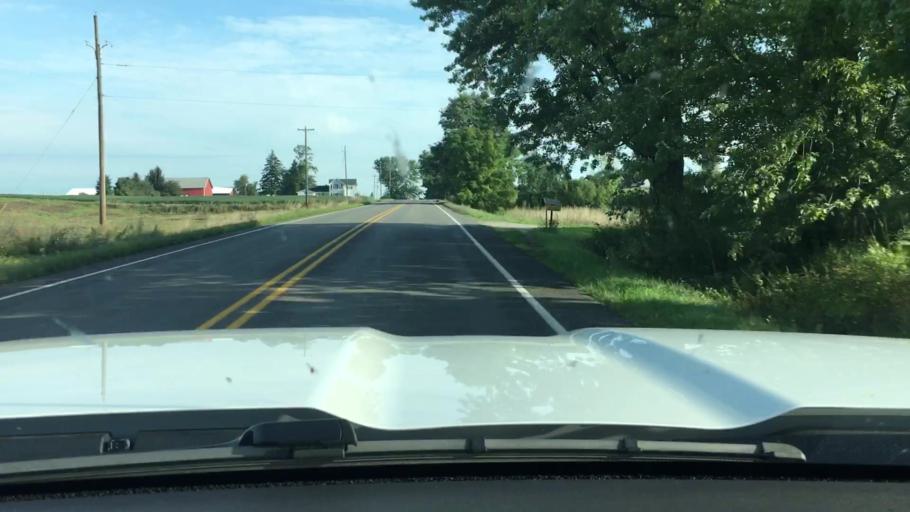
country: US
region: Michigan
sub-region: Kent County
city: Kent City
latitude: 43.1969
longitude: -85.7707
